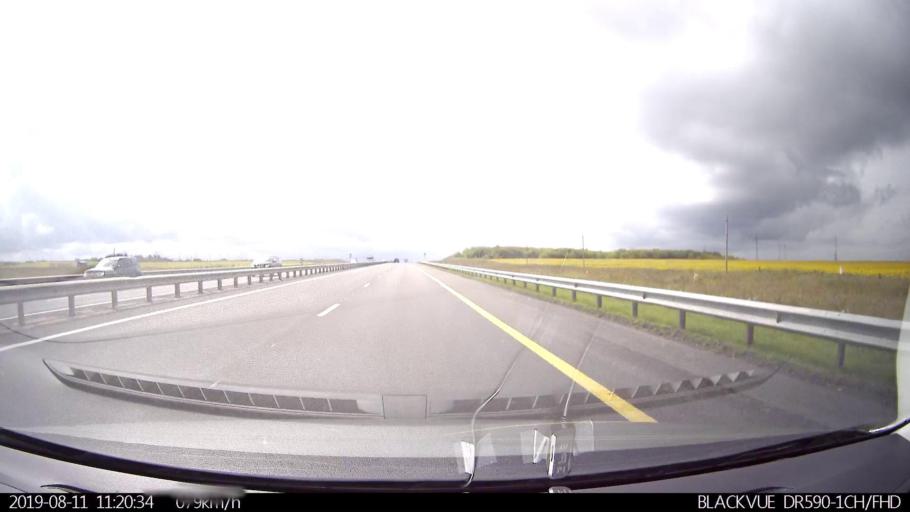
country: RU
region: Ulyanovsk
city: Novoul'yanovsk
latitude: 54.1563
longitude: 48.2644
